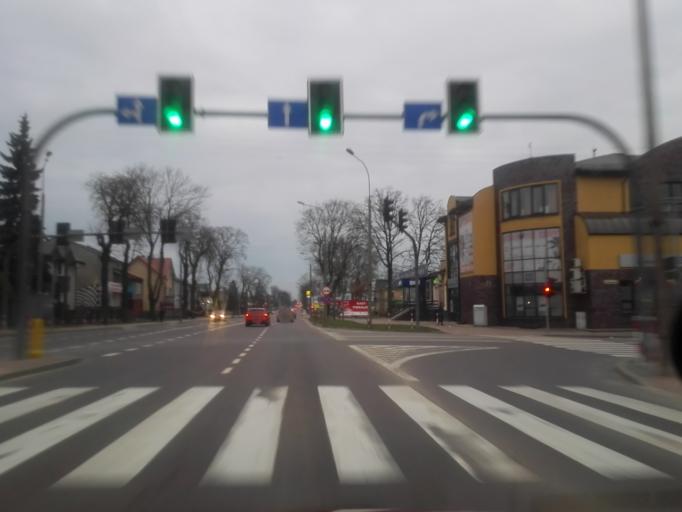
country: PL
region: Podlasie
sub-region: Lomza
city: Lomza
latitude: 53.1718
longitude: 22.0670
